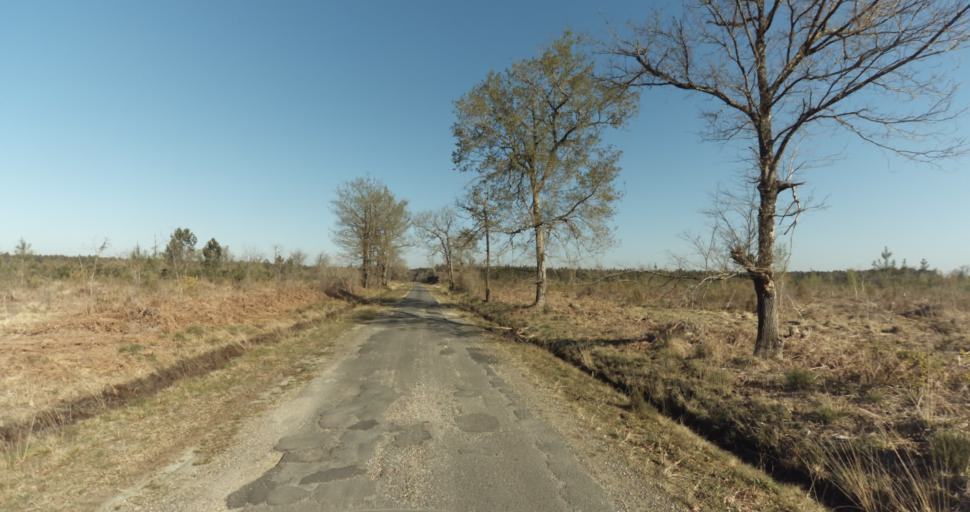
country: FR
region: Aquitaine
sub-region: Departement de la Gironde
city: Martignas-sur-Jalle
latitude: 44.8092
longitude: -0.8507
